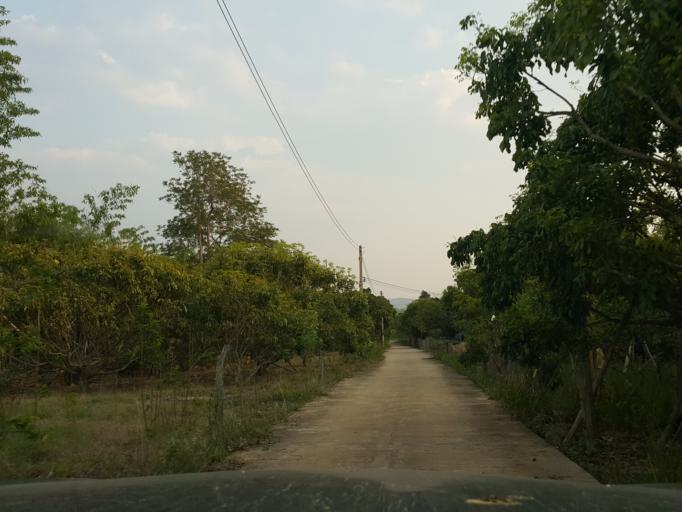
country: TH
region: Lamphun
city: Li
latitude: 17.8640
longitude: 99.0303
